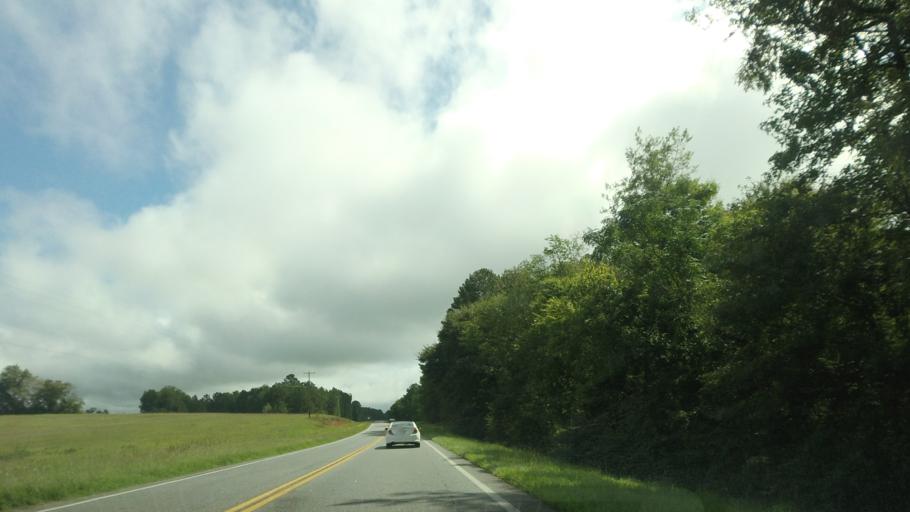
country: US
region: Georgia
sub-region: Laurens County
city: Dublin
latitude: 32.5468
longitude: -83.0166
